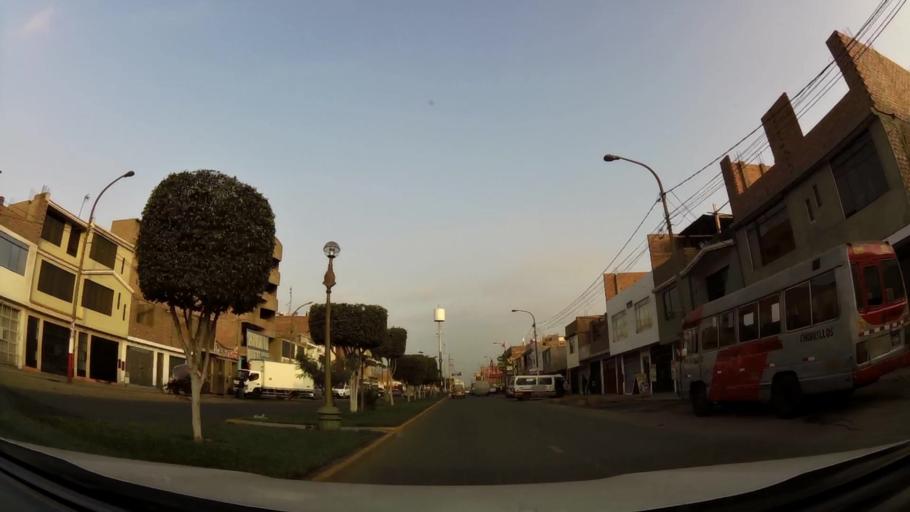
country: PE
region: Callao
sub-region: Callao
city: Callao
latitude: -12.0002
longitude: -77.1067
